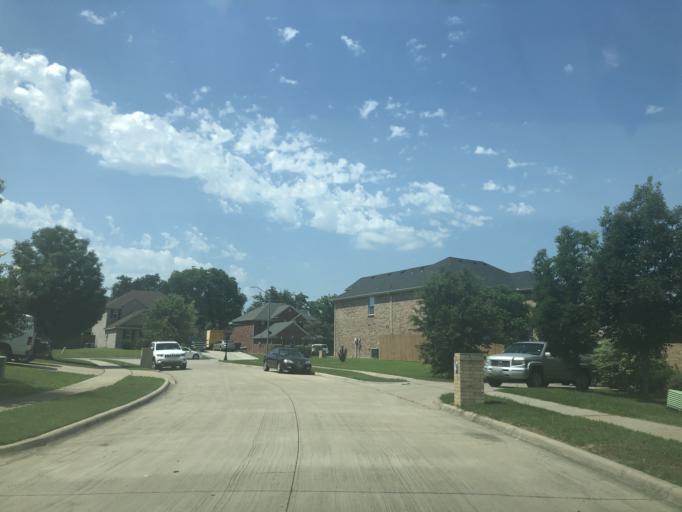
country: US
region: Texas
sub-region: Dallas County
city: Grand Prairie
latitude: 32.7257
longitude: -97.0020
